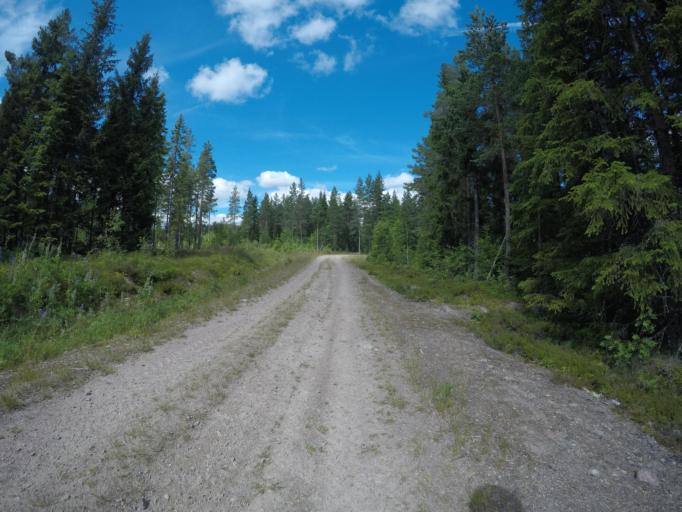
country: SE
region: Vaermland
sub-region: Filipstads Kommun
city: Lesjofors
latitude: 60.0762
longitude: 14.4582
